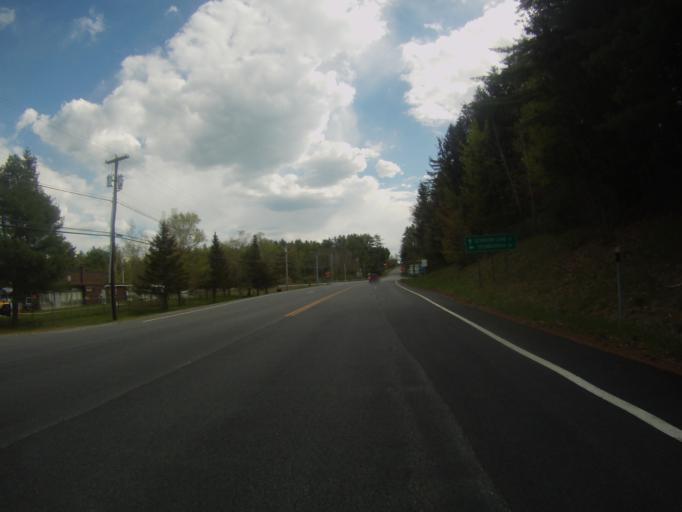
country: US
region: New York
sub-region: Essex County
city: Mineville
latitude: 43.8721
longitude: -73.7516
